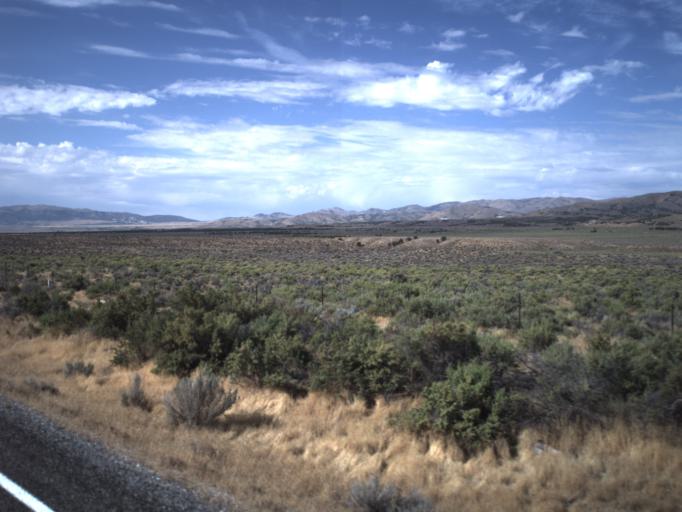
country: US
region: Idaho
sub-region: Cassia County
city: Burley
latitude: 41.6619
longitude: -113.5474
